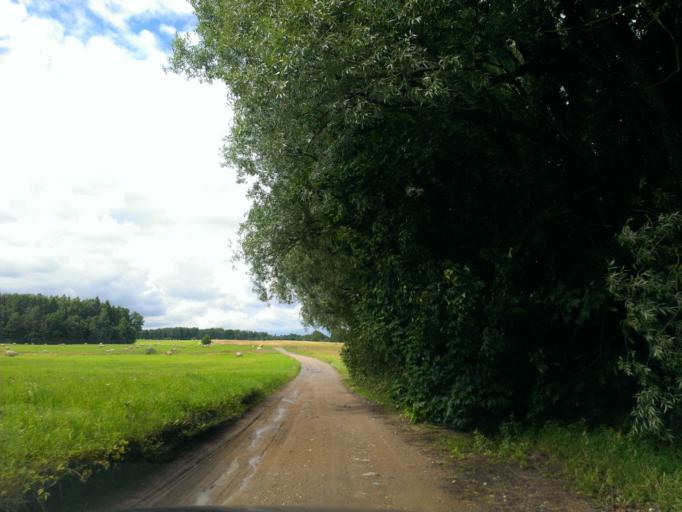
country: LV
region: Ligatne
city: Ligatne
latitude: 57.2238
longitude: 25.0045
